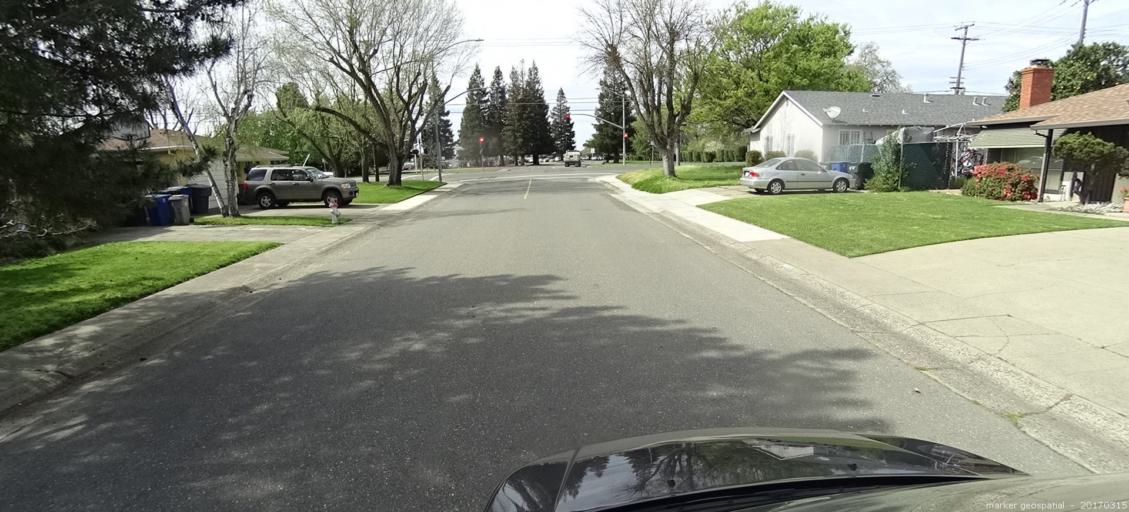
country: US
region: California
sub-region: Sacramento County
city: Parkway
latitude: 38.5207
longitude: -121.4825
